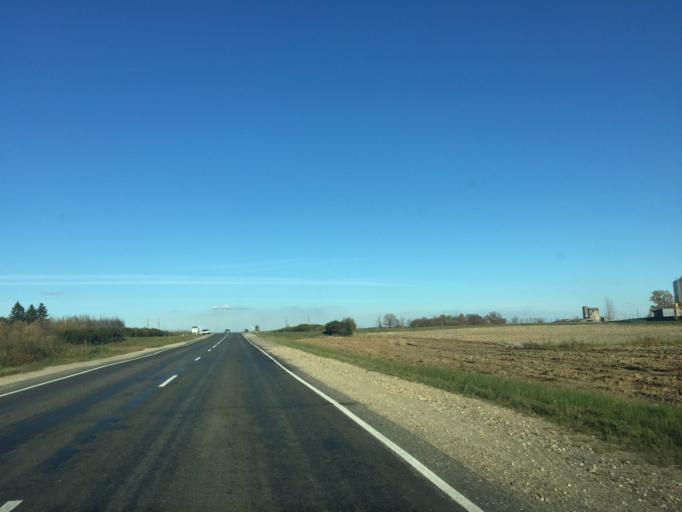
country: BY
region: Vitebsk
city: Dzisna
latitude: 55.3360
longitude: 28.2837
